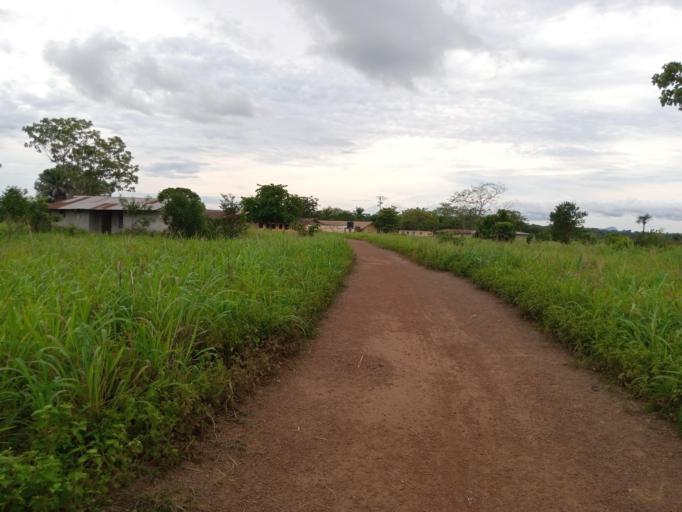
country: SL
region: Southern Province
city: Largo
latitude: 8.1131
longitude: -12.0604
